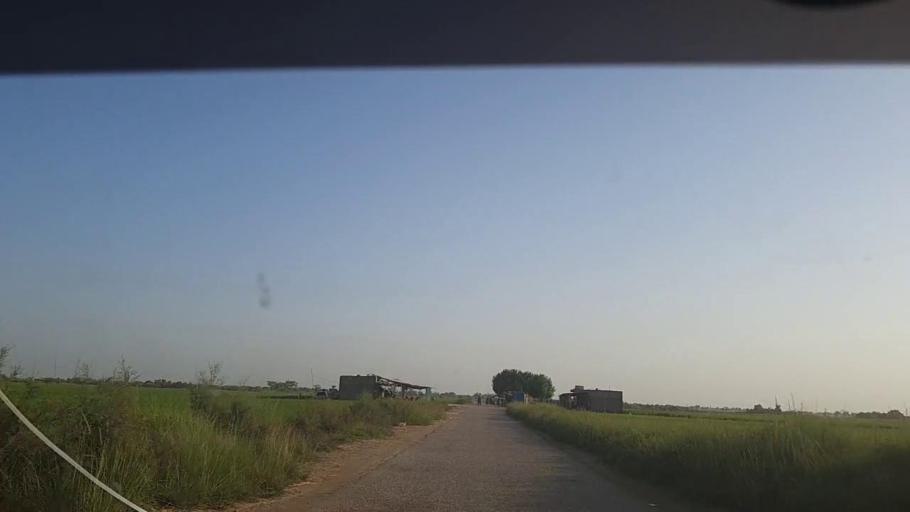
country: PK
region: Sindh
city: Thul
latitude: 28.1969
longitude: 68.8738
